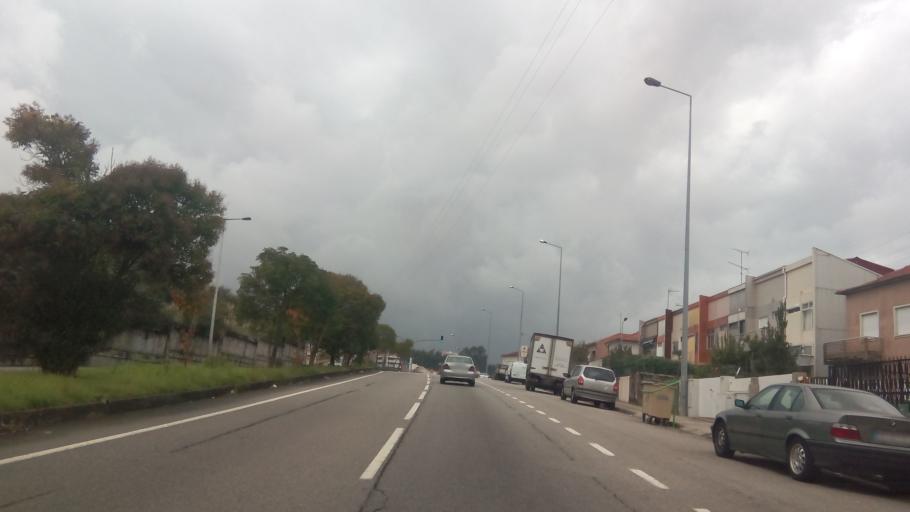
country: PT
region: Porto
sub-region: Gondomar
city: Rio Tinto
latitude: 41.1776
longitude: -8.5681
